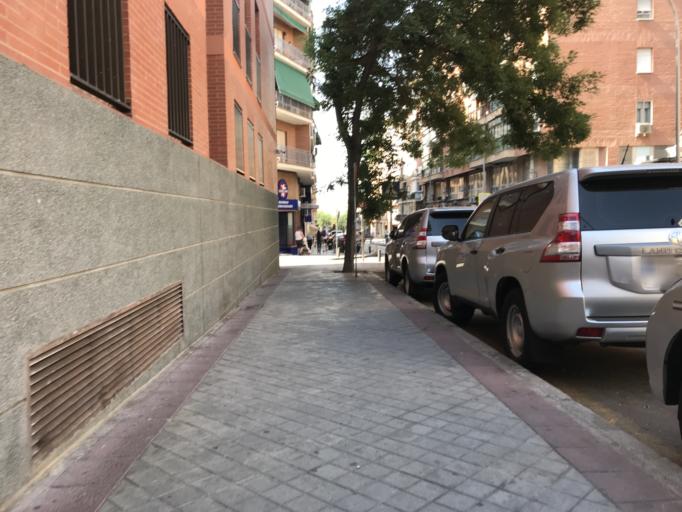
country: ES
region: Madrid
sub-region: Provincia de Madrid
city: Arganzuela
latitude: 40.3996
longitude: -3.6963
